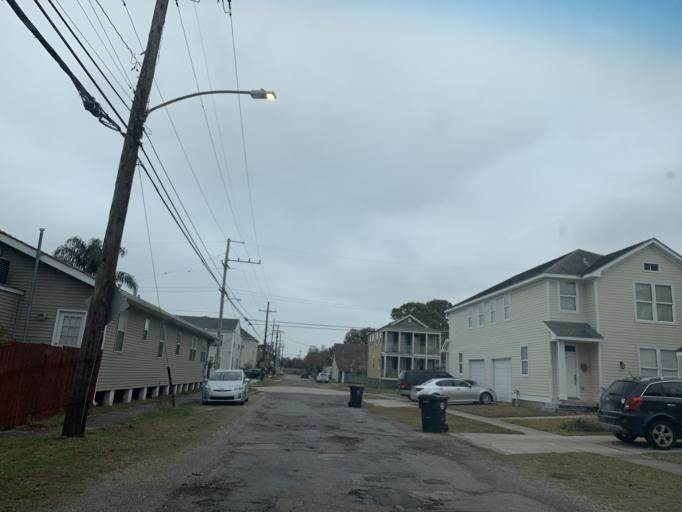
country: US
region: Louisiana
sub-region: Jefferson Parish
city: Metairie
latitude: 29.9899
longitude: -90.1068
